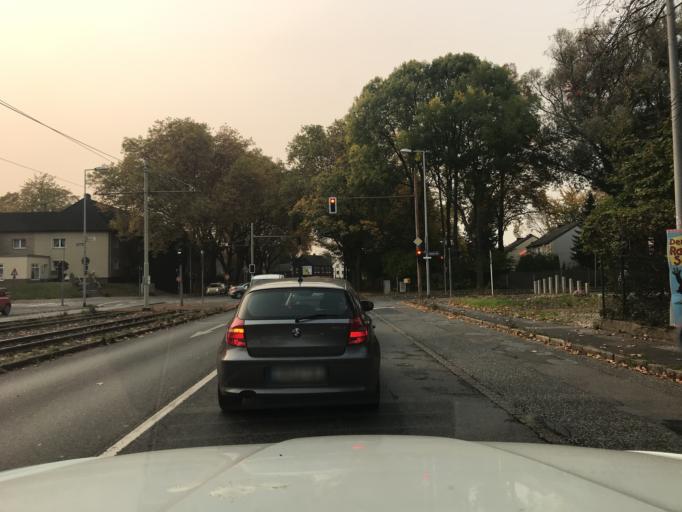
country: DE
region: North Rhine-Westphalia
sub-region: Regierungsbezirk Dusseldorf
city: Muelheim (Ruhr)
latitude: 51.4153
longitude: 6.9096
